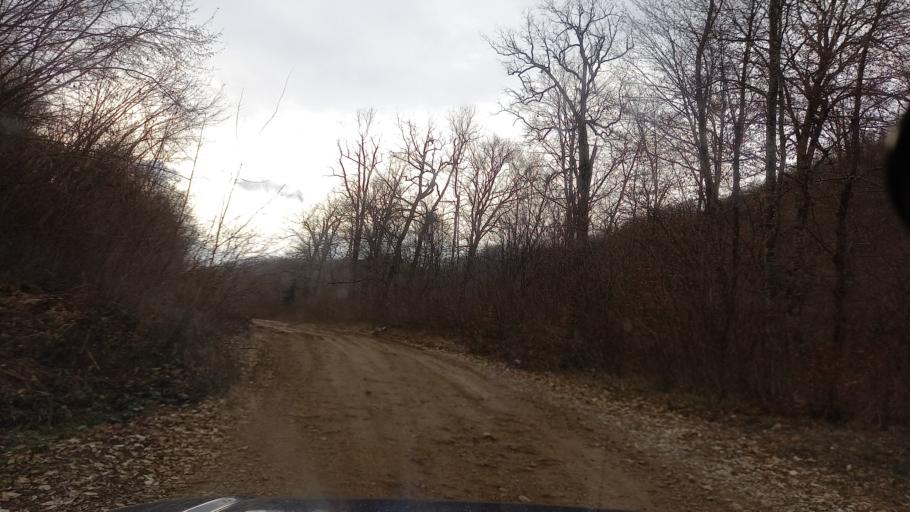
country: RU
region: Adygeya
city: Kamennomostskiy
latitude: 44.1715
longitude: 40.2984
